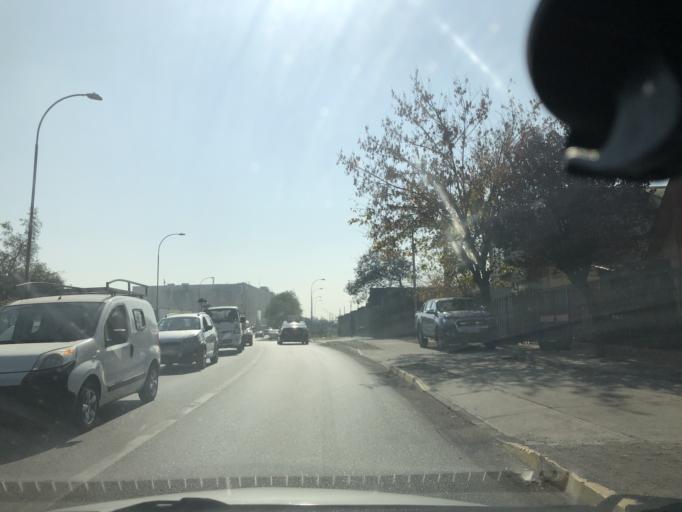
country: CL
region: Santiago Metropolitan
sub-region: Provincia de Cordillera
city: Puente Alto
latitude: -33.6023
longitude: -70.5737
